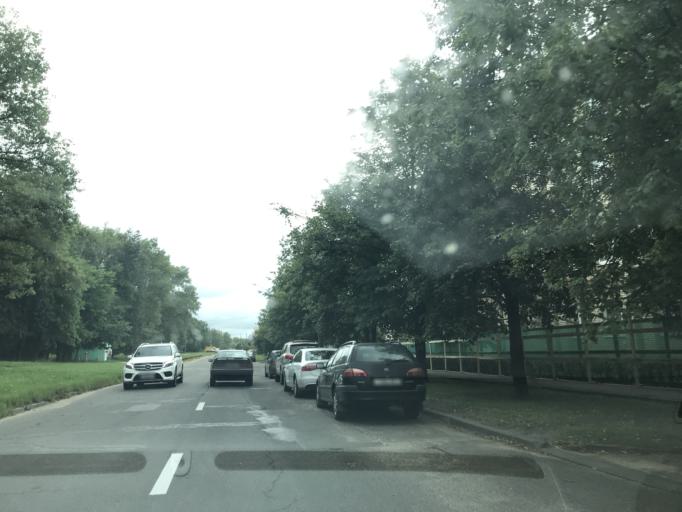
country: BY
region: Minsk
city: Minsk
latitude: 53.9416
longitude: 27.6106
